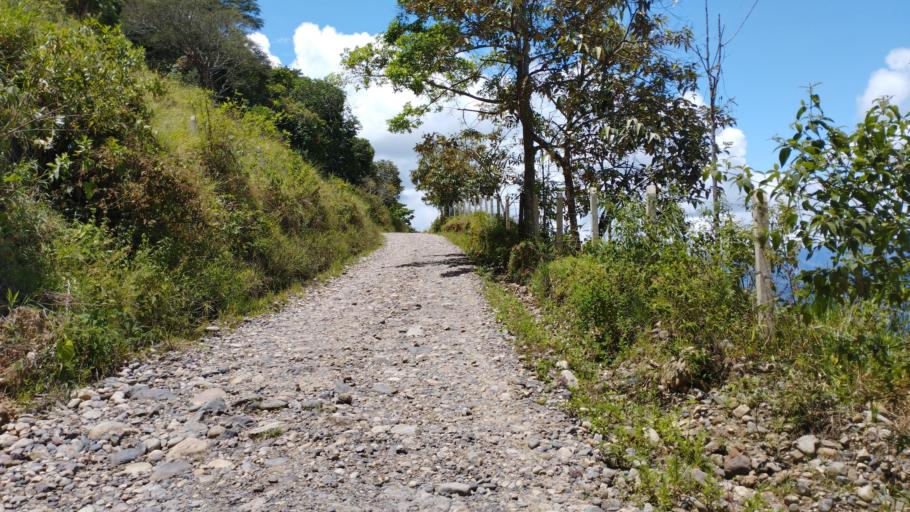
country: CO
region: Boyaca
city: San Luis de Gaceno
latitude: 4.7488
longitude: -73.1434
